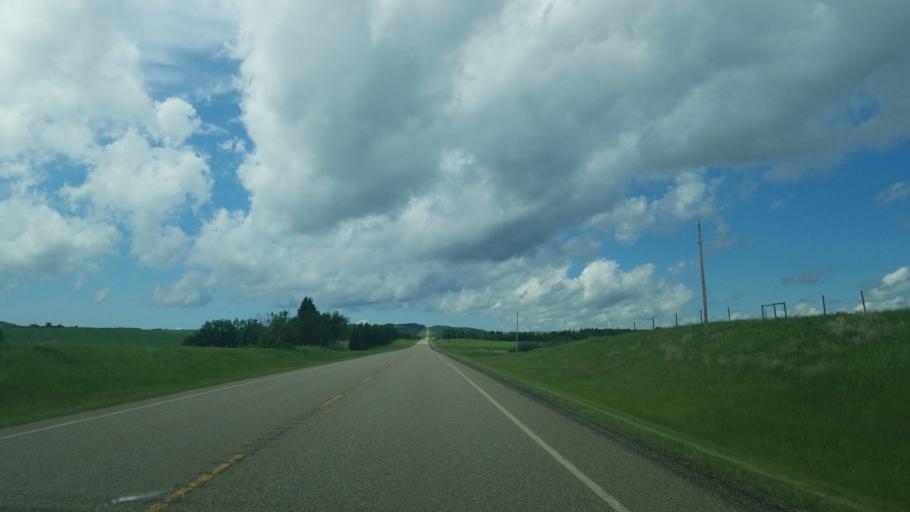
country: CA
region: Saskatchewan
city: Lloydminster
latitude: 53.1616
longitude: -110.1853
